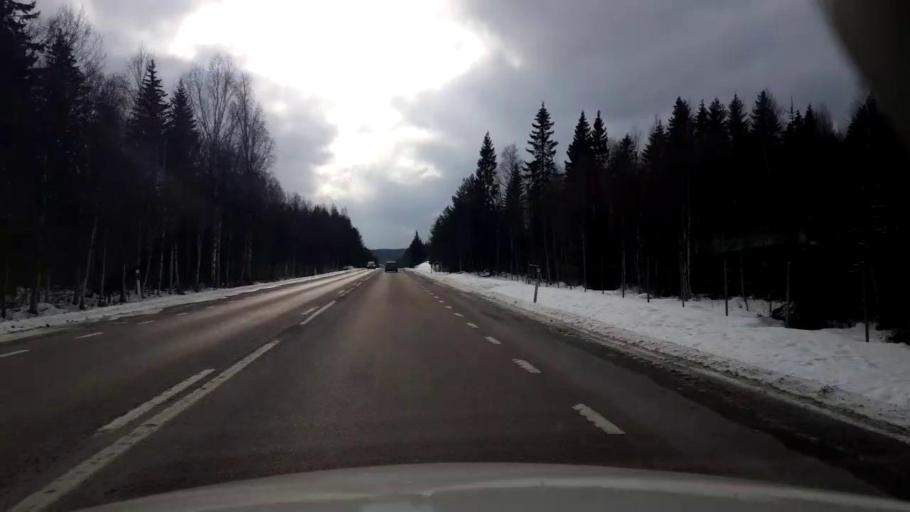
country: SE
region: Gaevleborg
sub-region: Nordanstigs Kommun
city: Bergsjoe
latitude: 61.9452
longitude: 17.2251
